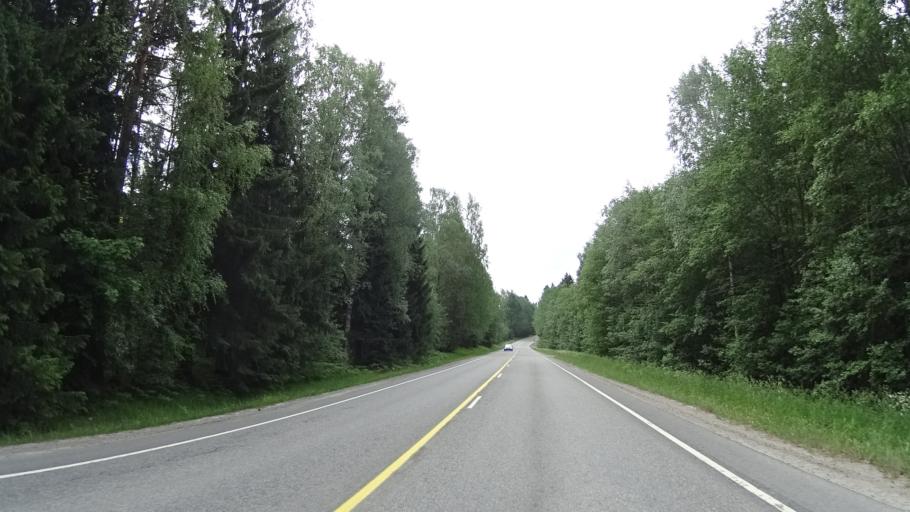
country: FI
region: Uusimaa
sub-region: Helsinki
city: Vihti
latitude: 60.2867
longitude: 24.4065
